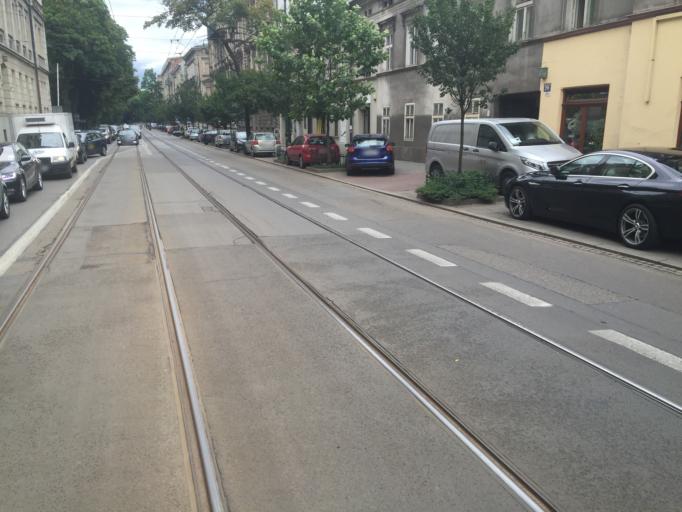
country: PL
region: Lesser Poland Voivodeship
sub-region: Krakow
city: Krakow
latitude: 50.0550
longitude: 19.9400
